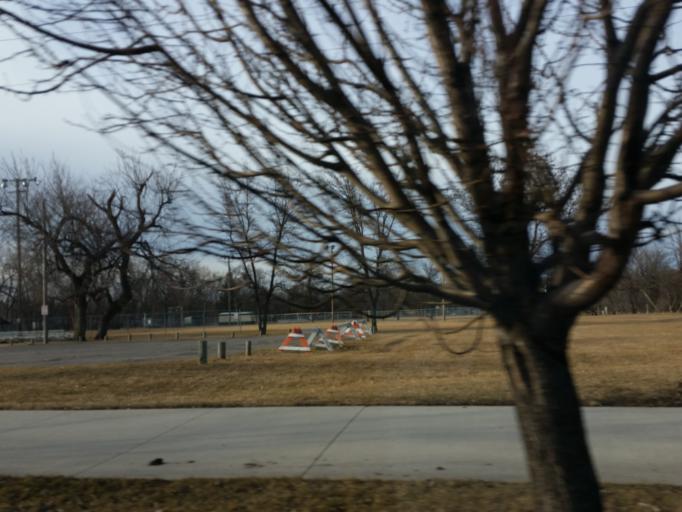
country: US
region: North Dakota
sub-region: Cass County
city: West Fargo
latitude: 46.8625
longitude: -96.9080
